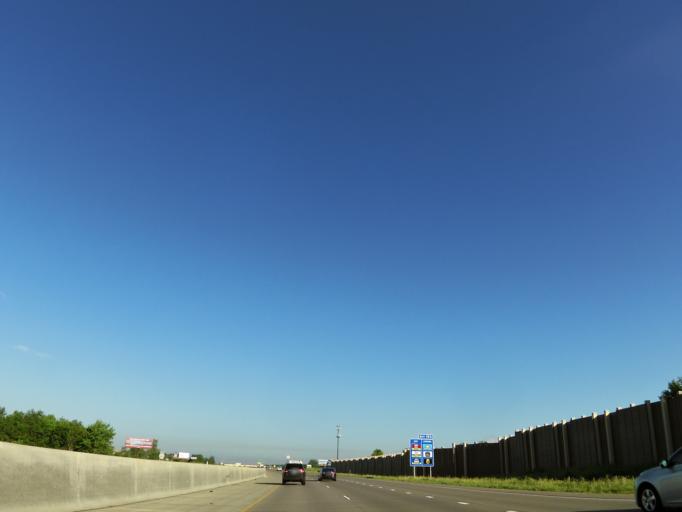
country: US
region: Minnesota
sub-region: Wright County
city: Monticello
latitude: 45.2961
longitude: -93.7859
